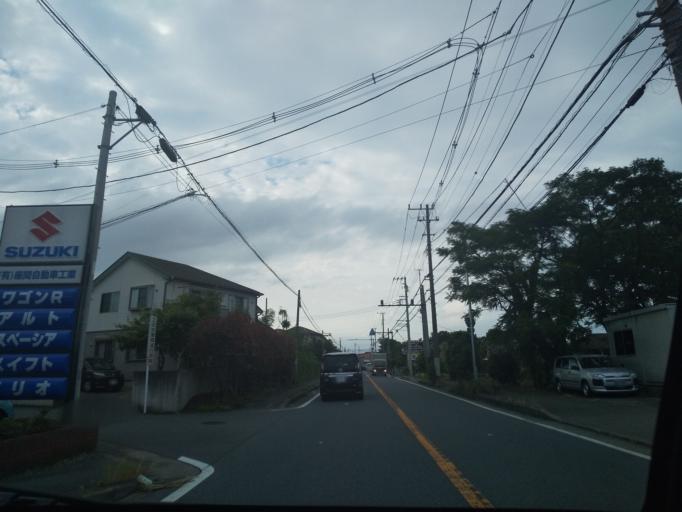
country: JP
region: Kanagawa
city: Zama
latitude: 35.4724
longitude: 139.3888
